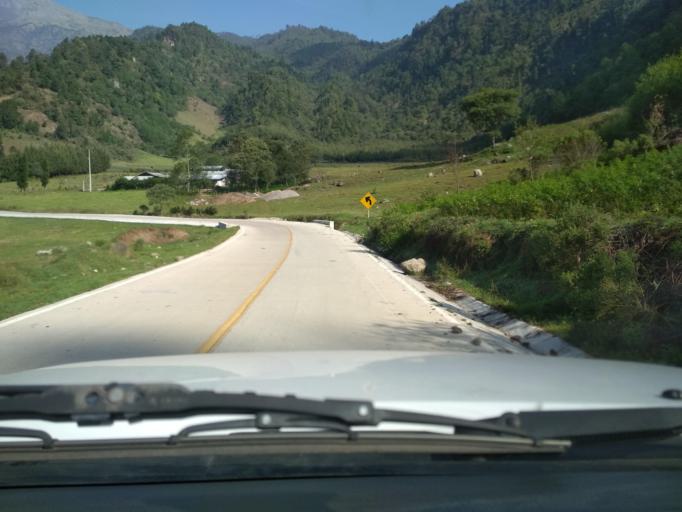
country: MX
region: Veracruz
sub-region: La Perla
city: Chilapa
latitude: 19.0055
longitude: -97.1807
